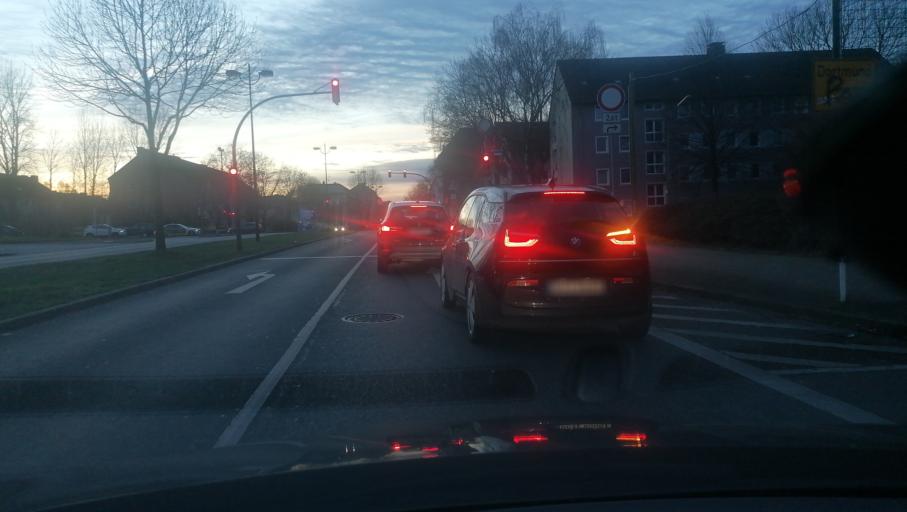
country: DE
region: North Rhine-Westphalia
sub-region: Regierungsbezirk Arnsberg
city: Dortmund
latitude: 51.5242
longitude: 7.4881
